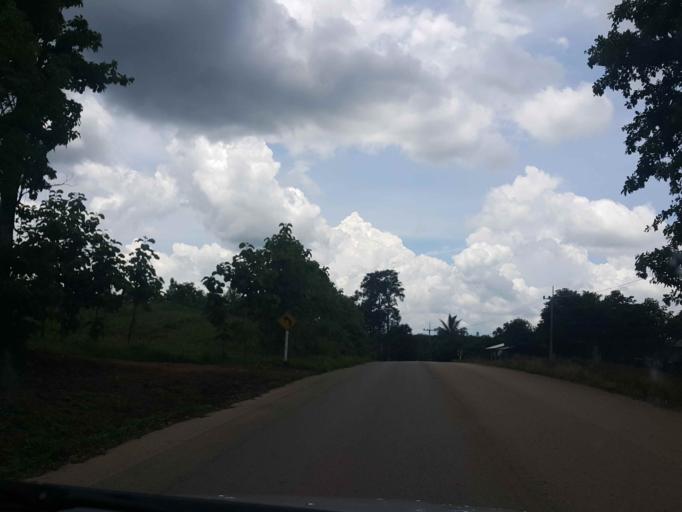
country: TH
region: Lampang
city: Ngao
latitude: 18.9536
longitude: 100.0751
